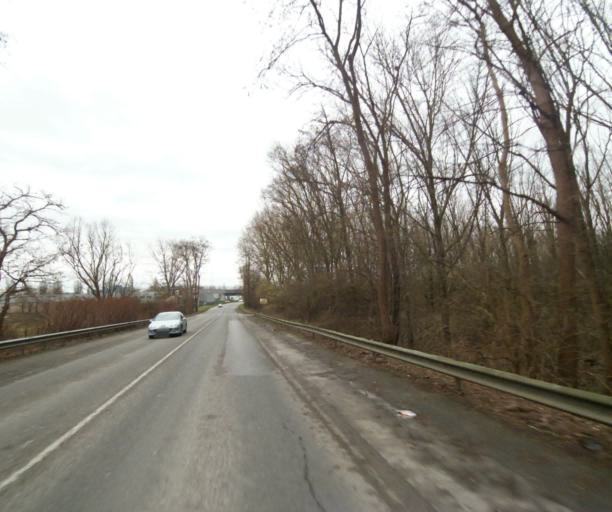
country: FR
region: Nord-Pas-de-Calais
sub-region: Departement du Nord
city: Bruay-sur-l'Escaut
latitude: 50.3901
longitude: 3.5452
